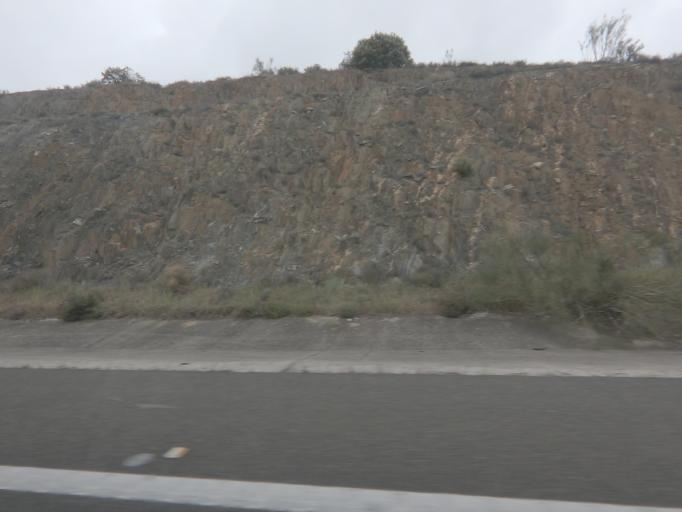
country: ES
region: Extremadura
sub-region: Provincia de Caceres
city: Santiago del Campo
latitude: 39.6215
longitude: -6.4017
